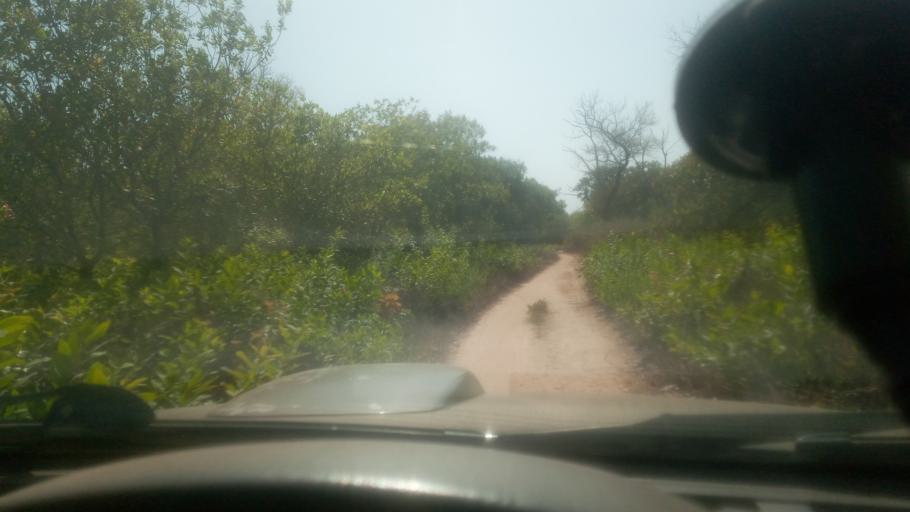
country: GW
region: Oio
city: Farim
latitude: 12.4537
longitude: -15.4143
